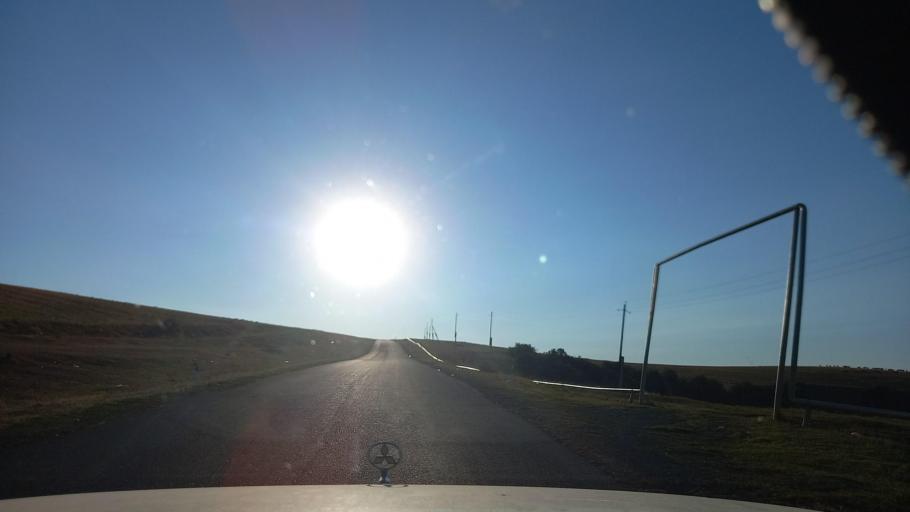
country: AZ
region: Shamkir Rayon
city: Shamkhor
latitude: 40.7661
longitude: 45.9502
